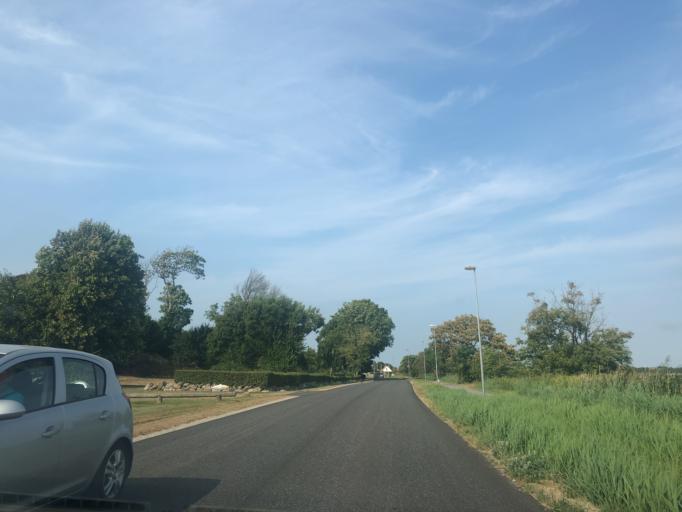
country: DK
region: North Denmark
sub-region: Morso Kommune
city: Nykobing Mors
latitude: 56.8127
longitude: 9.0229
